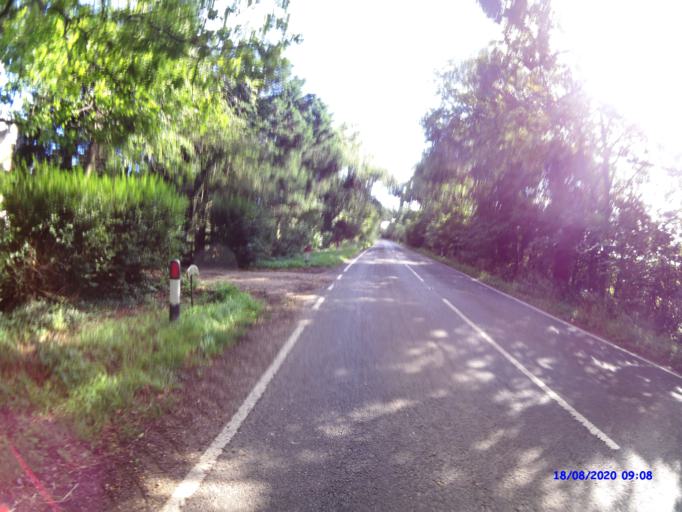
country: GB
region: England
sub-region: Cambridgeshire
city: Ramsey
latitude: 52.4680
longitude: -0.0948
